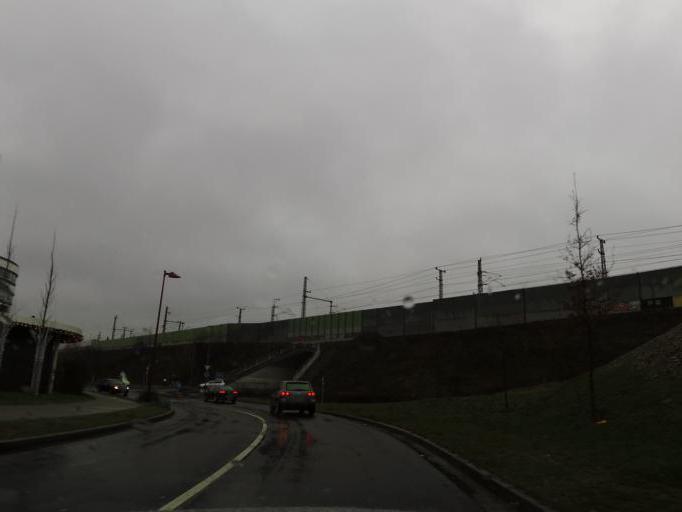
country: DE
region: Rheinland-Pfalz
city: Montabaur
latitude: 50.4440
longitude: 7.8314
